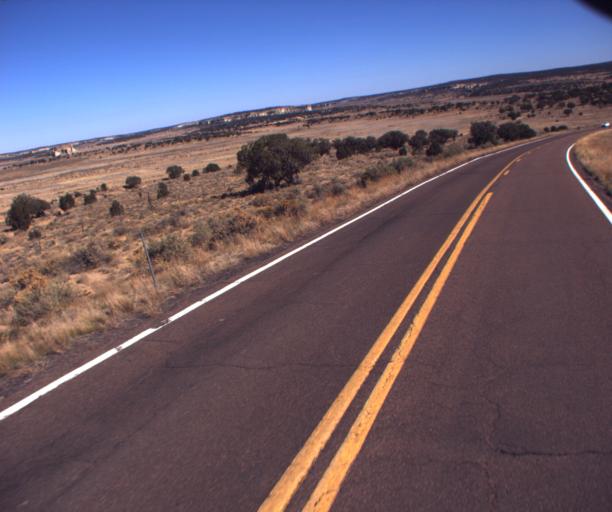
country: US
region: Arizona
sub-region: Apache County
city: Ganado
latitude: 35.7545
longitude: -109.8982
